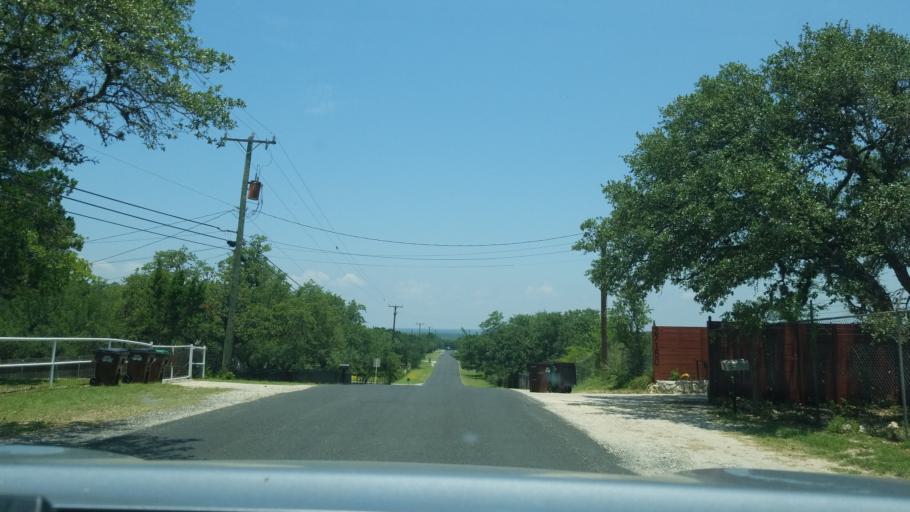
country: US
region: Texas
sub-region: Bexar County
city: Timberwood Park
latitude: 29.7020
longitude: -98.5166
